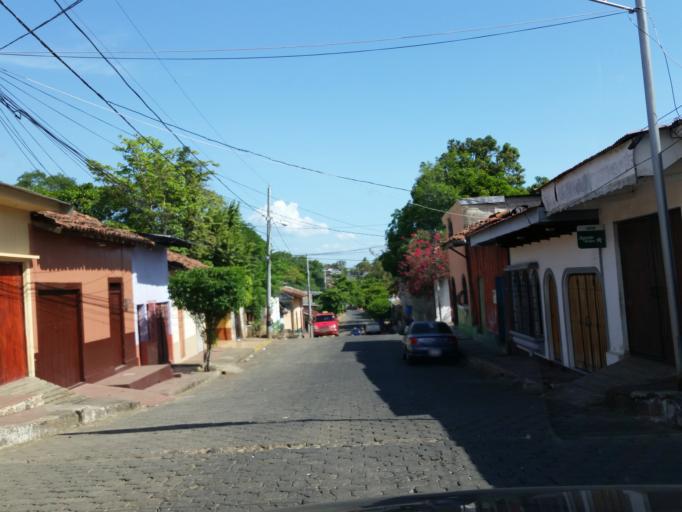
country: NI
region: Leon
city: Leon
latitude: 12.4342
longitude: -86.8745
